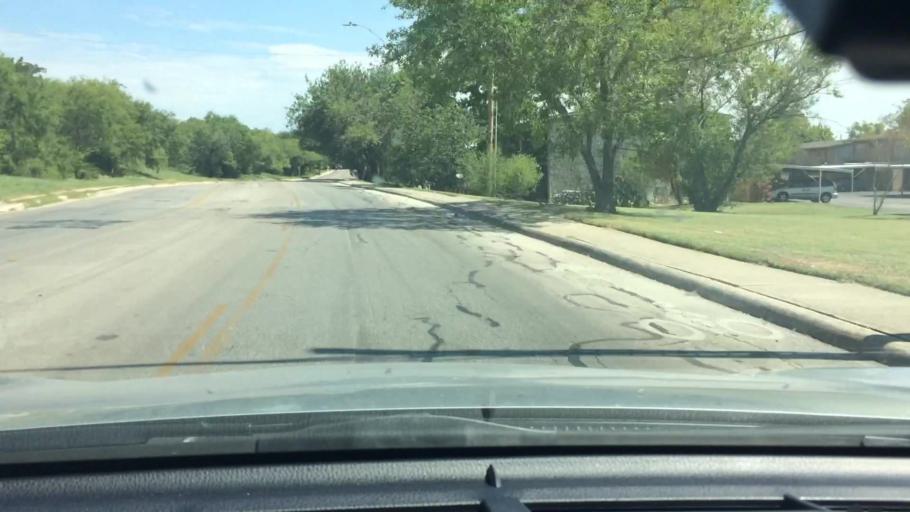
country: US
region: Texas
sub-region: Bexar County
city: San Antonio
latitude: 29.3791
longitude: -98.4315
